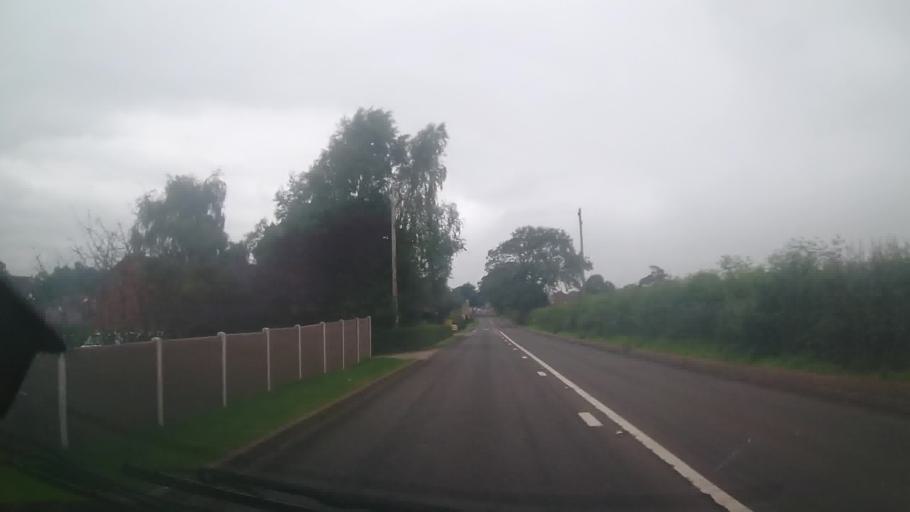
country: GB
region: England
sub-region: Shropshire
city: Whitchurch
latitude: 52.9545
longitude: -2.6719
